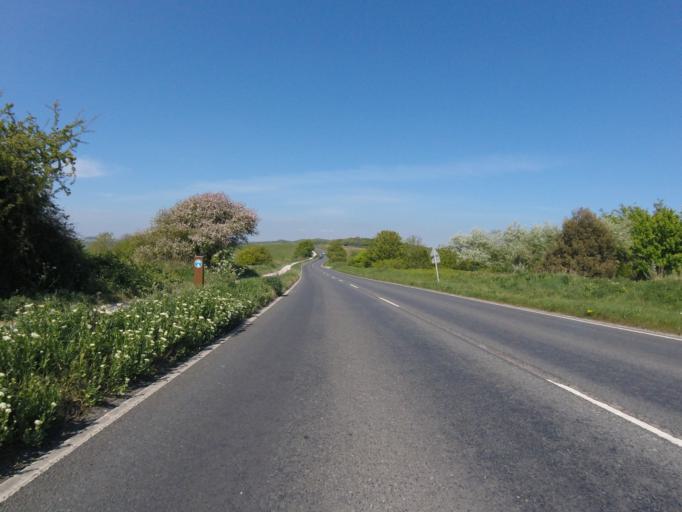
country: GB
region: England
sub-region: Brighton and Hove
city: Brighton
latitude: 50.8613
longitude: -0.1211
